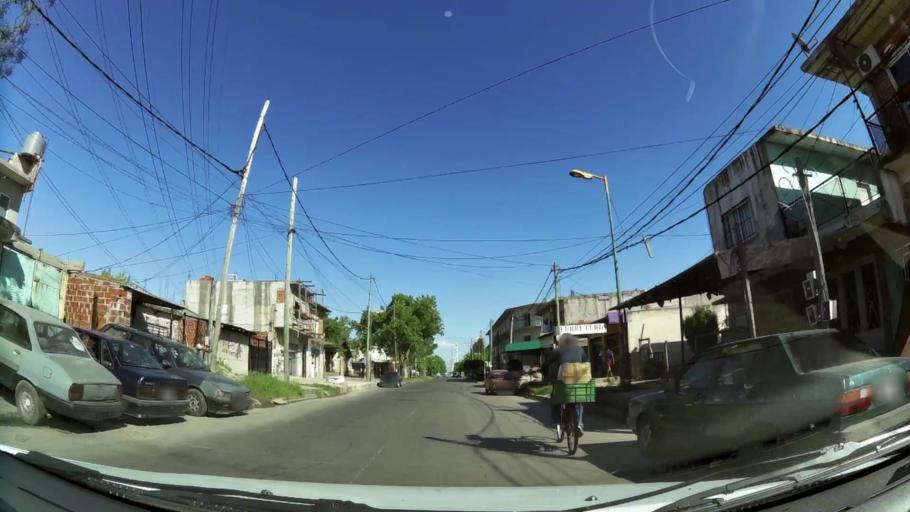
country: AR
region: Buenos Aires
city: Caseros
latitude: -34.5538
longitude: -58.5936
